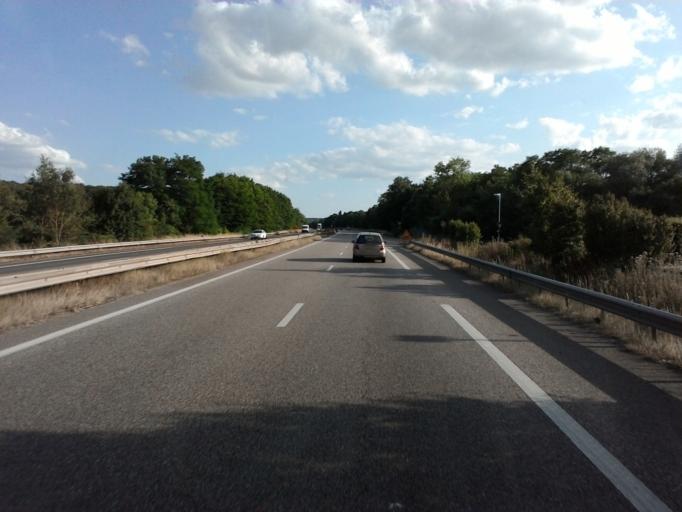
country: FR
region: Lorraine
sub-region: Departement de Meurthe-et-Moselle
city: Richardmenil
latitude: 48.6061
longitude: 6.1739
